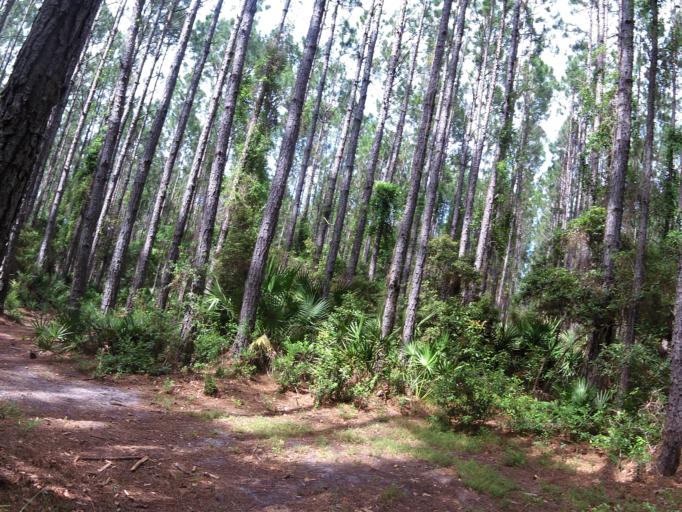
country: US
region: Florida
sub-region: Duval County
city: Atlantic Beach
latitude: 30.4536
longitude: -81.4754
